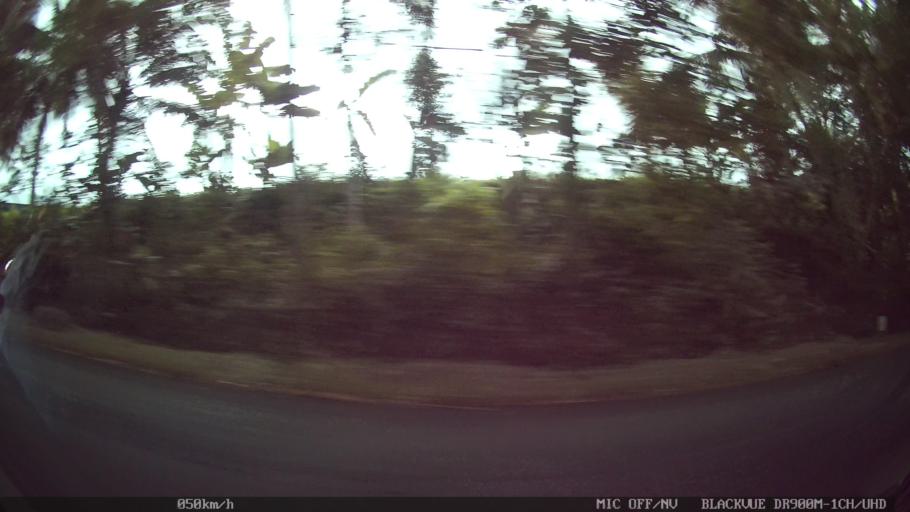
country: ID
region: Bali
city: Banjar Sempidi
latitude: -8.5238
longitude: 115.1983
